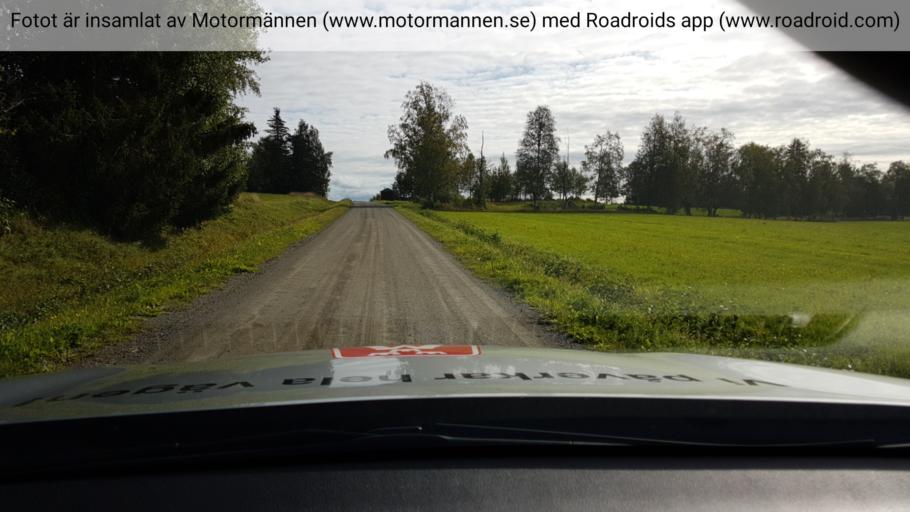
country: SE
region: Jaemtland
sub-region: Bergs Kommun
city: Hoverberg
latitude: 62.9357
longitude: 14.4187
